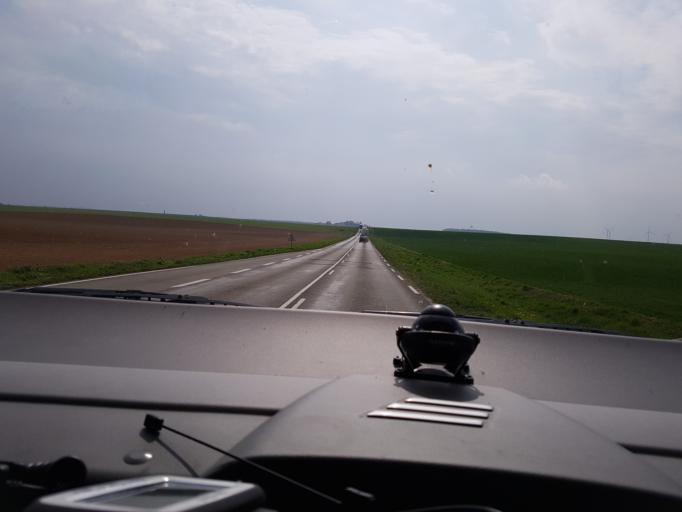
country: FR
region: Picardie
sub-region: Departement de l'Aisne
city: Coucy-le-Chateau-Auffrique
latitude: 49.4652
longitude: 3.3486
